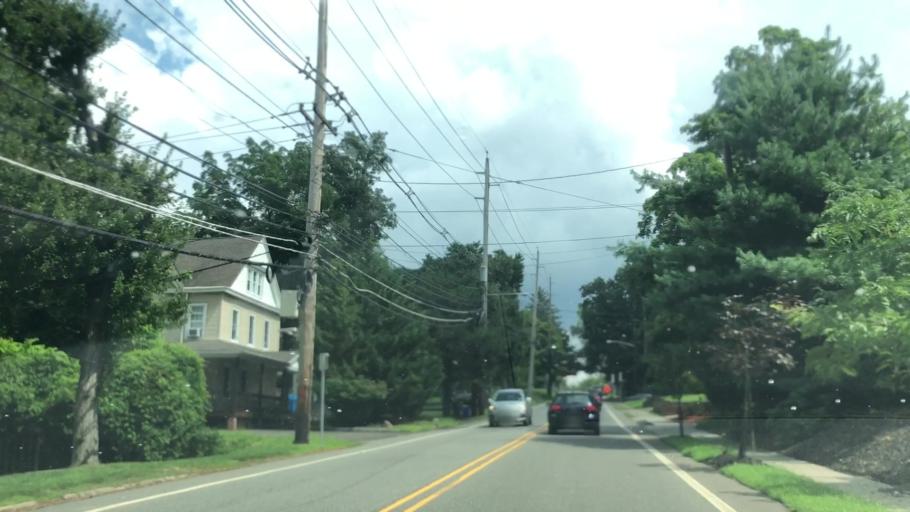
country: US
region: New Jersey
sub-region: Passaic County
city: Little Falls
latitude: 40.8749
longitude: -74.2092
